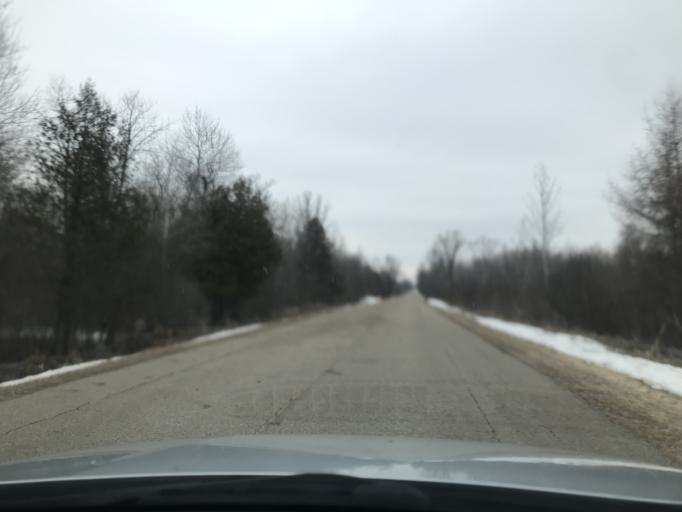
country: US
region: Wisconsin
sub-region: Marinette County
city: Peshtigo
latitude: 45.1313
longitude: -88.0075
